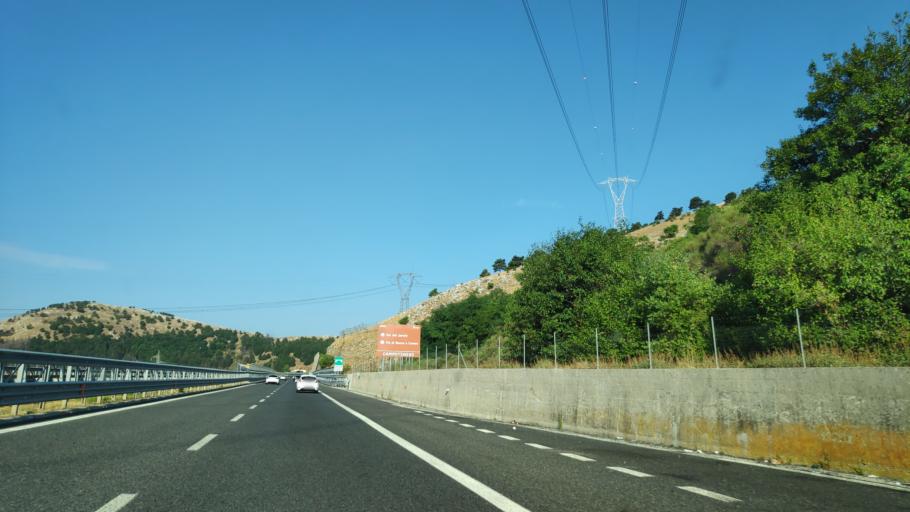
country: IT
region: Calabria
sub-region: Provincia di Cosenza
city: Morano Calabro
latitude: 39.8684
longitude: 16.1113
